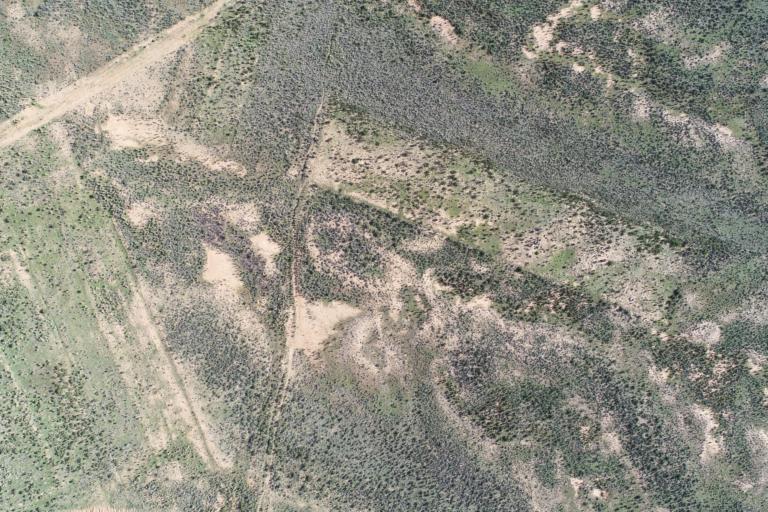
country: BO
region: La Paz
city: Curahuara de Carangas
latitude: -17.2979
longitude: -68.4961
